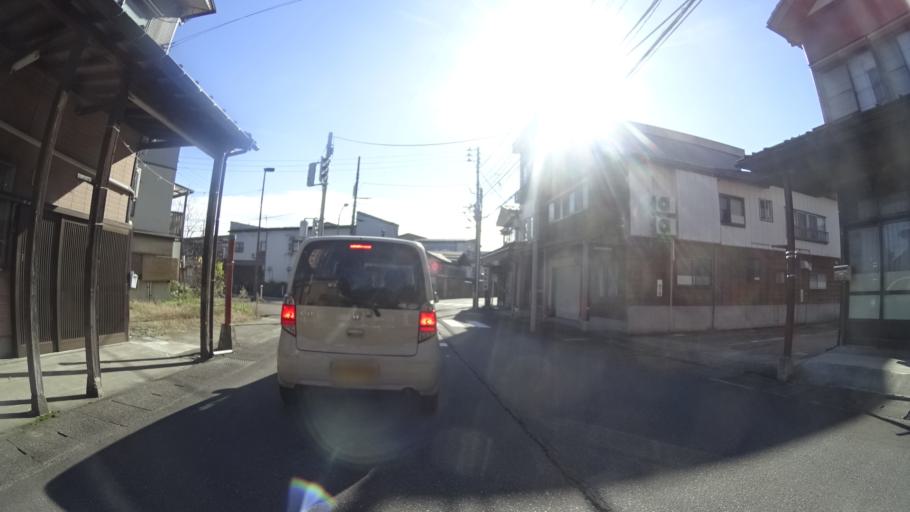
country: JP
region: Niigata
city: Tochio-honcho
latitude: 37.4796
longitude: 138.9909
